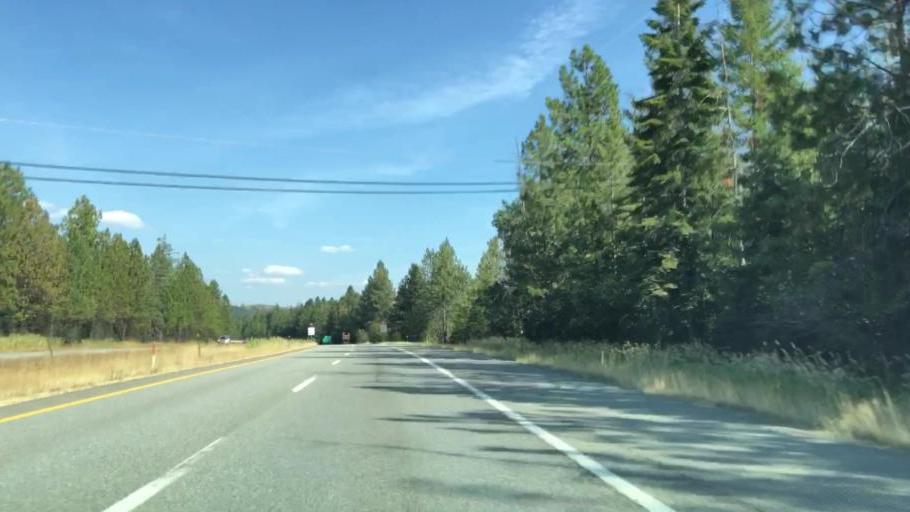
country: US
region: Idaho
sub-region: Shoshone County
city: Pinehurst
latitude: 47.5506
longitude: -116.3024
